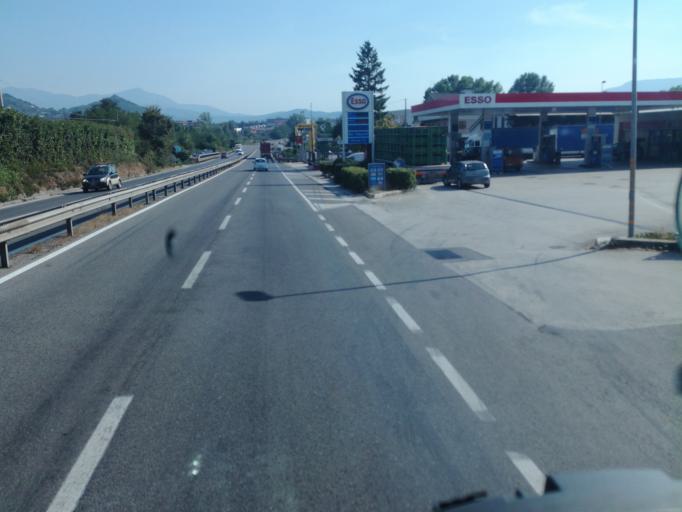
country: IT
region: Campania
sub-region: Provincia di Avellino
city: Atripalda
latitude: 40.9326
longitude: 14.8310
